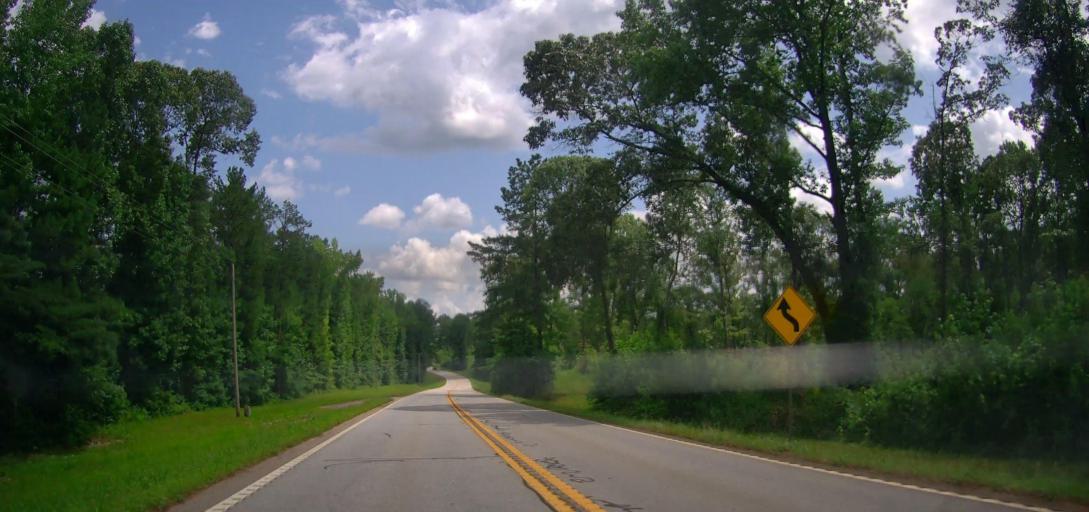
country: US
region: Georgia
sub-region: Heard County
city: Franklin
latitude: 33.3059
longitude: -85.1388
